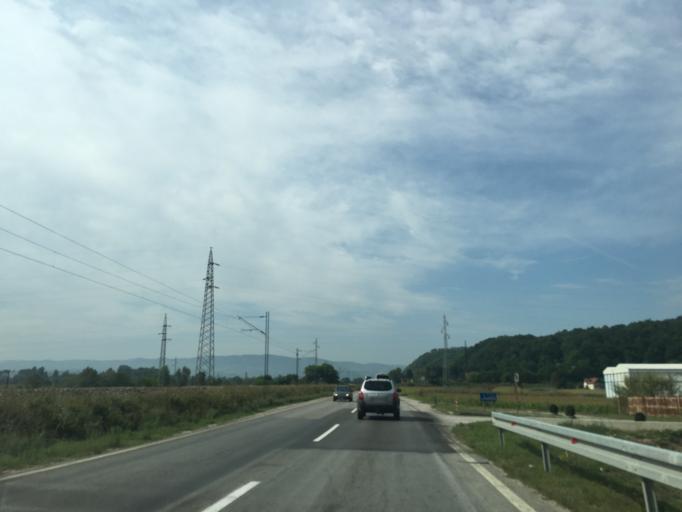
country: RS
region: Central Serbia
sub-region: Zlatiborski Okrug
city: Pozega
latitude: 43.8609
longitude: 20.0858
